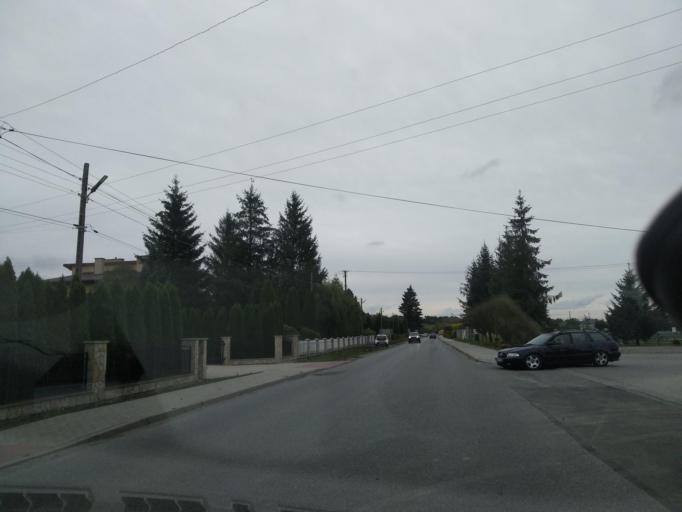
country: PL
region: Subcarpathian Voivodeship
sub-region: Powiat krosnienski
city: Miejsce Piastowe
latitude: 49.6131
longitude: 21.7536
